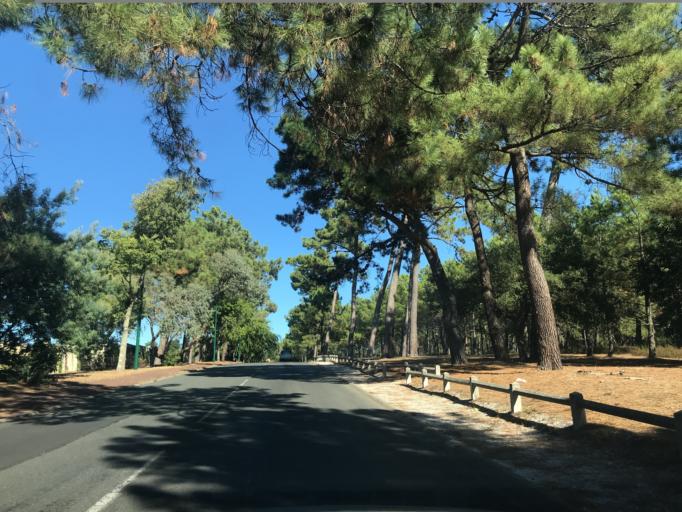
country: FR
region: Aquitaine
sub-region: Departement de la Gironde
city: Arcachon
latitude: 44.6536
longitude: -1.1807
